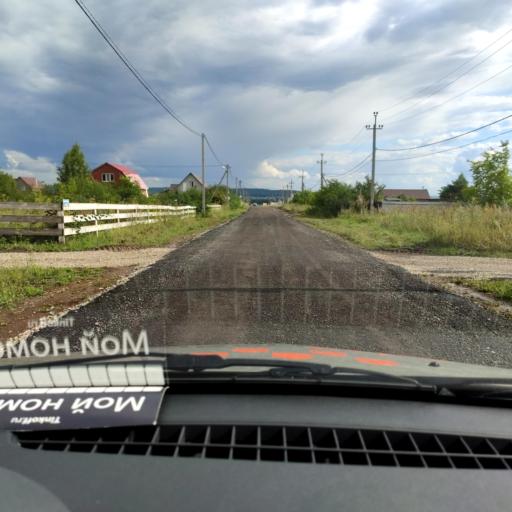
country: RU
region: Bashkortostan
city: Avdon
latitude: 54.5201
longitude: 55.8334
